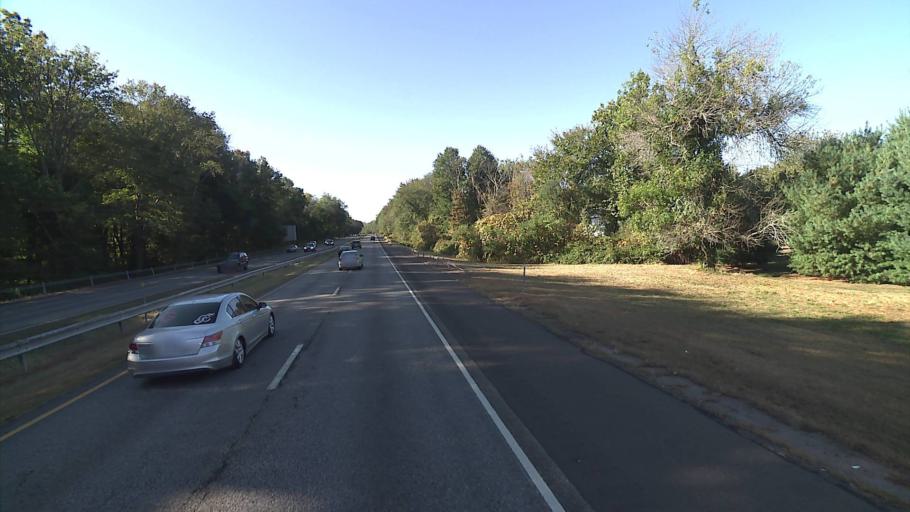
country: US
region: Connecticut
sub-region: New Haven County
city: Wallingford
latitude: 41.4449
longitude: -72.8445
